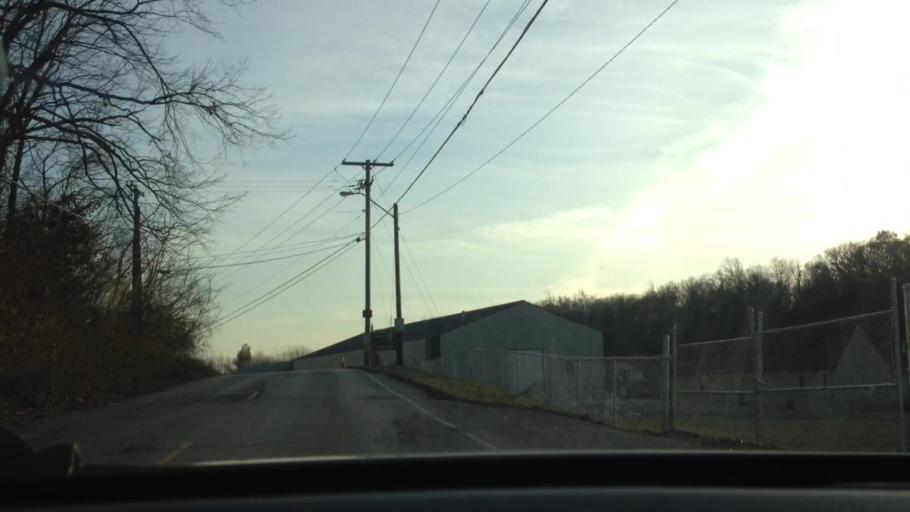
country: US
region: Missouri
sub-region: Clay County
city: North Kansas City
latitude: 39.1561
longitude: -94.5474
